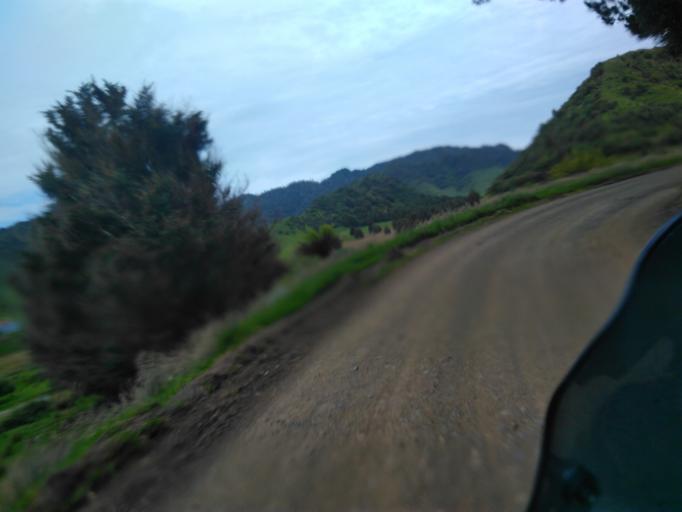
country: NZ
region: Bay of Plenty
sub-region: Opotiki District
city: Opotiki
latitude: -38.1051
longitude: 177.4967
